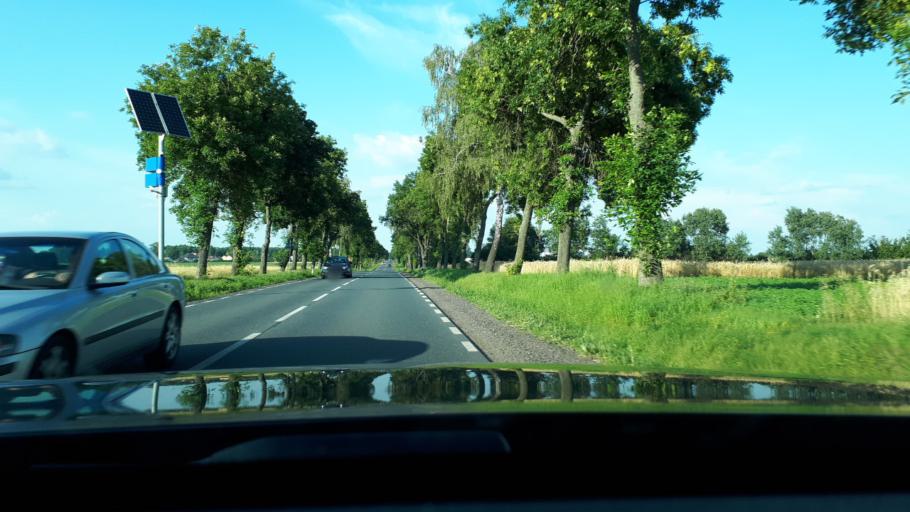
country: PL
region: Masovian Voivodeship
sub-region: Powiat ciechanowski
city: Ojrzen
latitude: 52.7960
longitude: 20.5841
